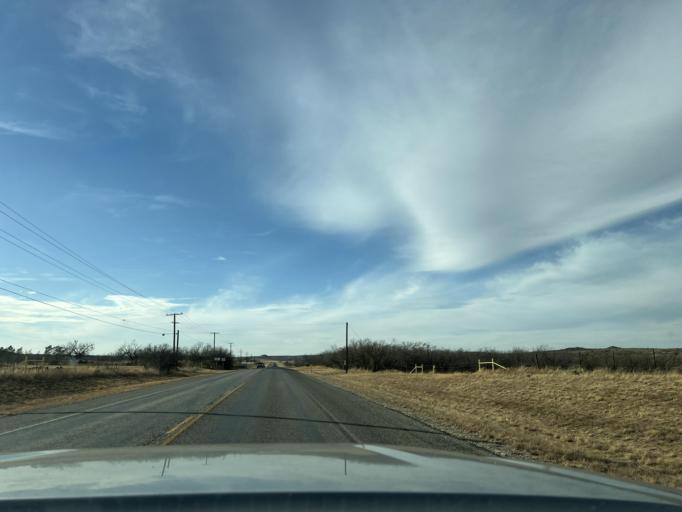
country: US
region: Texas
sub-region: Fisher County
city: Rotan
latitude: 32.7328
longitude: -100.6565
